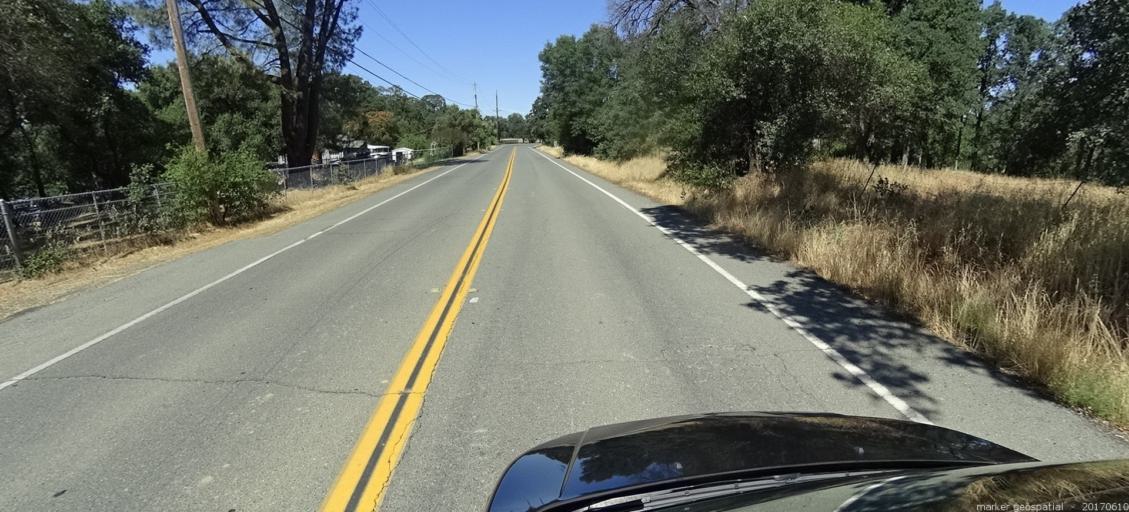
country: US
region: California
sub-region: Butte County
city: Oroville East
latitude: 39.5063
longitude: -121.5050
